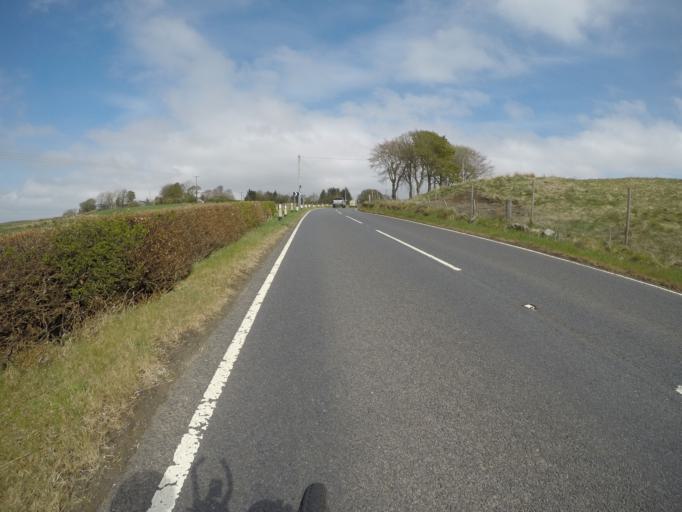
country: GB
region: Scotland
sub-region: East Renfrewshire
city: Neilston
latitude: 55.7245
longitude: -4.4266
